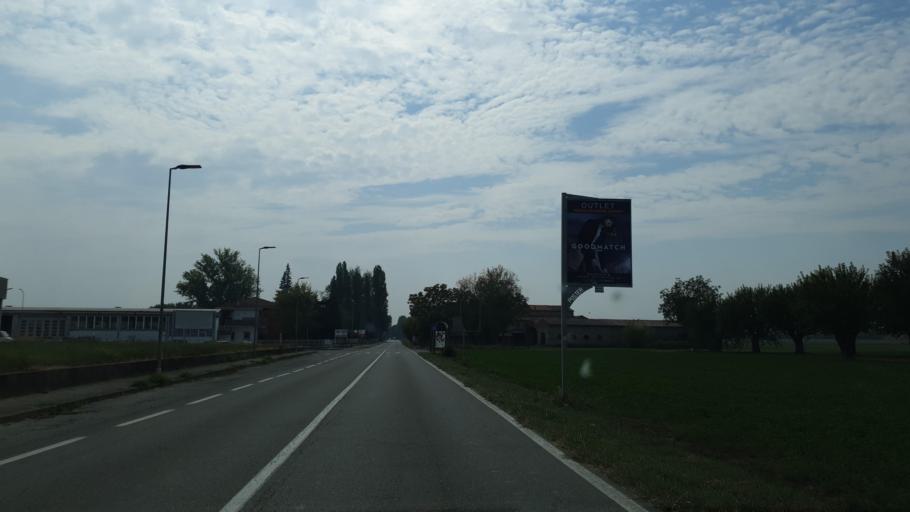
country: IT
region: Emilia-Romagna
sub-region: Provincia di Parma
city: San Secondo Parmense
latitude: 44.8807
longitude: 10.2549
